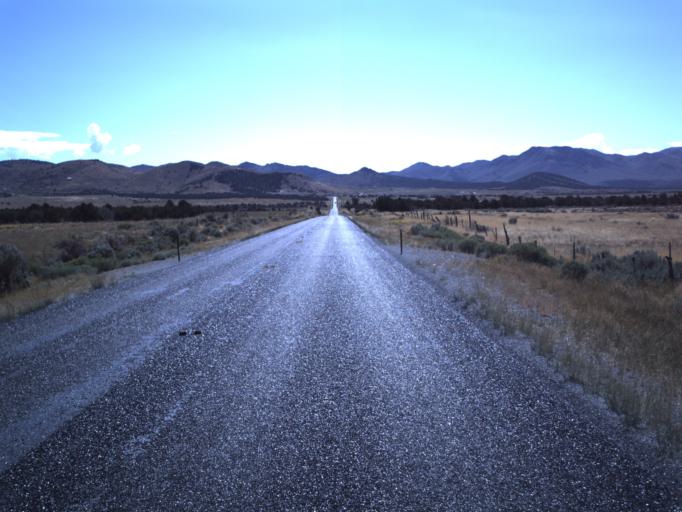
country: US
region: Utah
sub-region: Utah County
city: Genola
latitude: 39.9332
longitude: -112.1719
